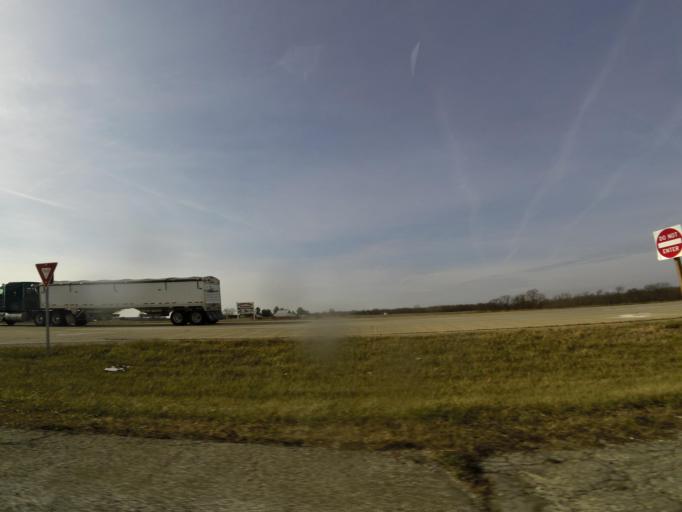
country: US
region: Illinois
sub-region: De Witt County
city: Clinton
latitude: 40.1484
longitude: -88.9853
